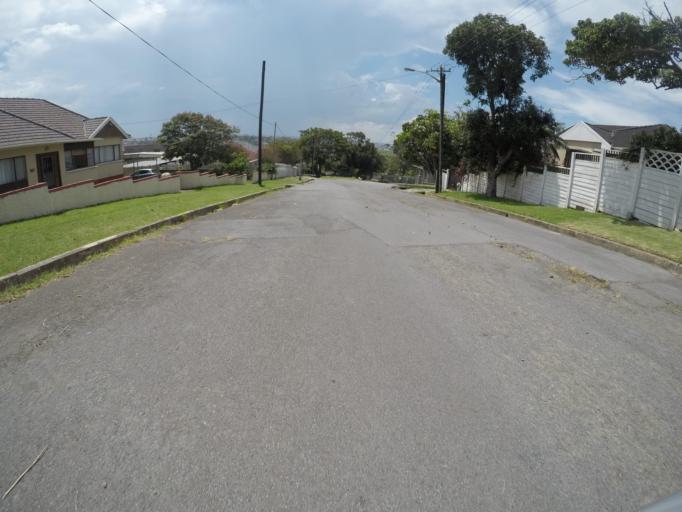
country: ZA
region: Eastern Cape
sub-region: Buffalo City Metropolitan Municipality
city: East London
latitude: -33.0317
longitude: 27.8633
